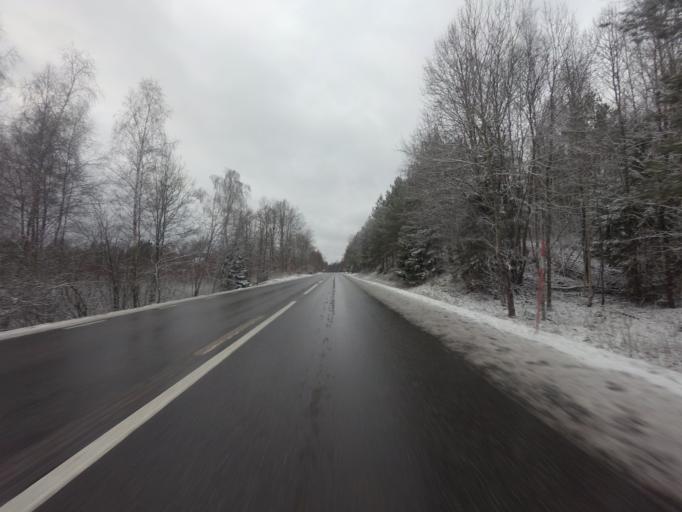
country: SE
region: Skane
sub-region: Osby Kommun
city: Lonsboda
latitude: 56.3933
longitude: 14.3006
